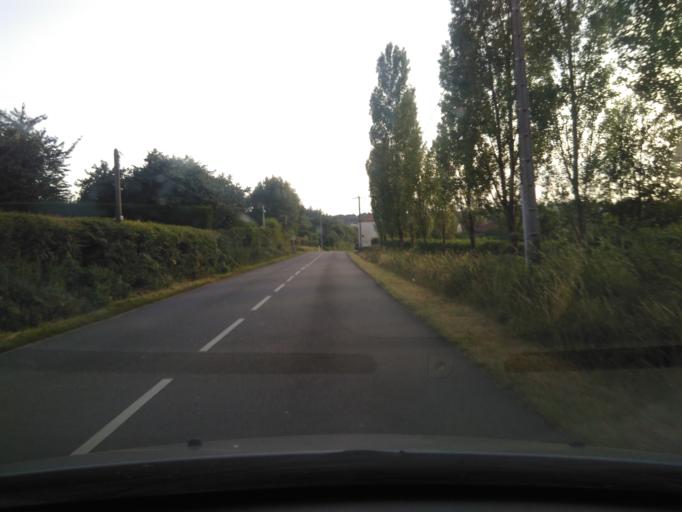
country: FR
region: Pays de la Loire
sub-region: Departement de la Vendee
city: Saint-Florent-des-Bois
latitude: 46.5847
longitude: -1.3555
